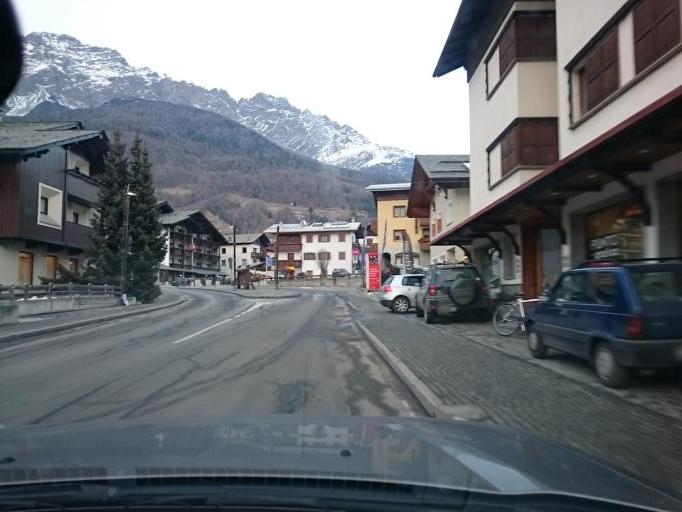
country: IT
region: Lombardy
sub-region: Provincia di Sondrio
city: Bormio
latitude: 46.4631
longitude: 10.3737
